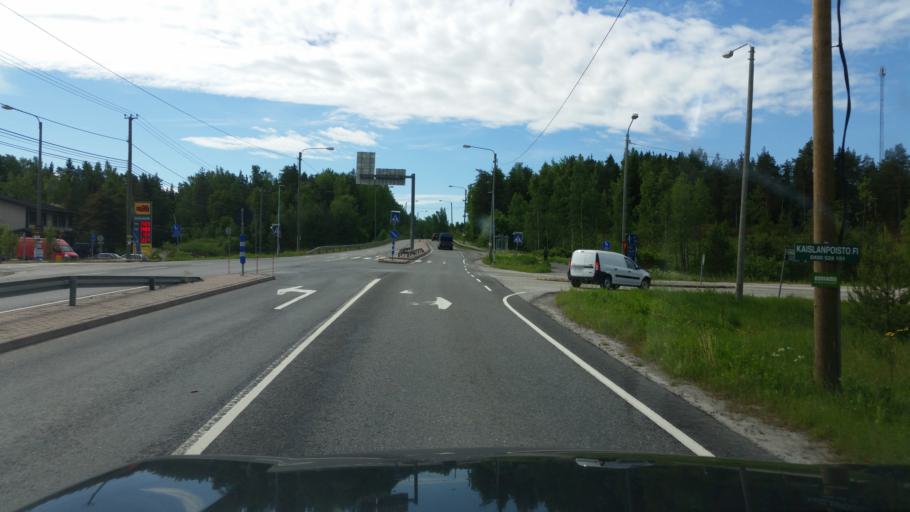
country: FI
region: Varsinais-Suomi
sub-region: Turku
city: Kaarina
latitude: 60.3390
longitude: 22.3645
